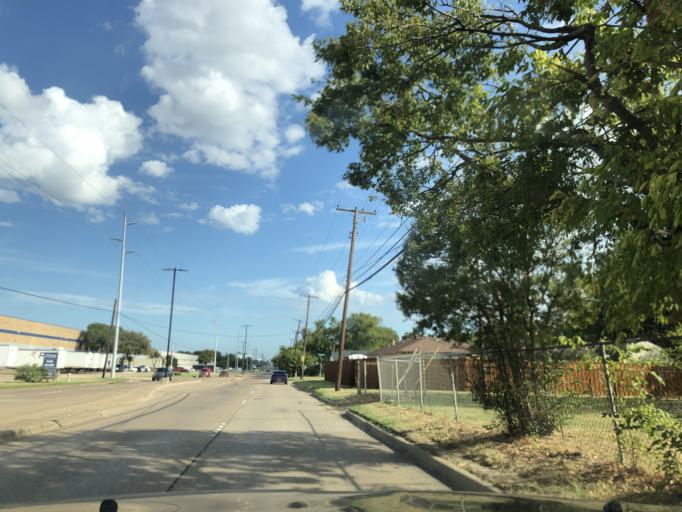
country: US
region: Texas
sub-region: Dallas County
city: Garland
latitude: 32.8817
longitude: -96.6654
